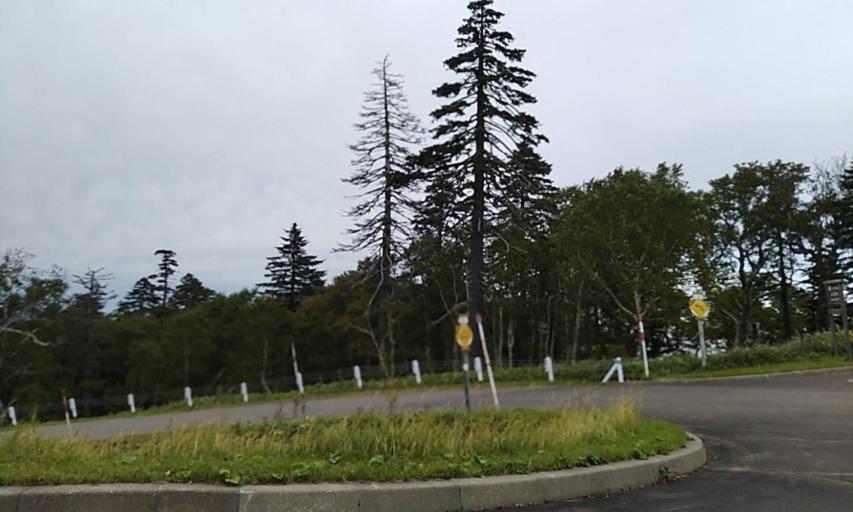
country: JP
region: Hokkaido
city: Bihoro
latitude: 43.5774
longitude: 144.2236
